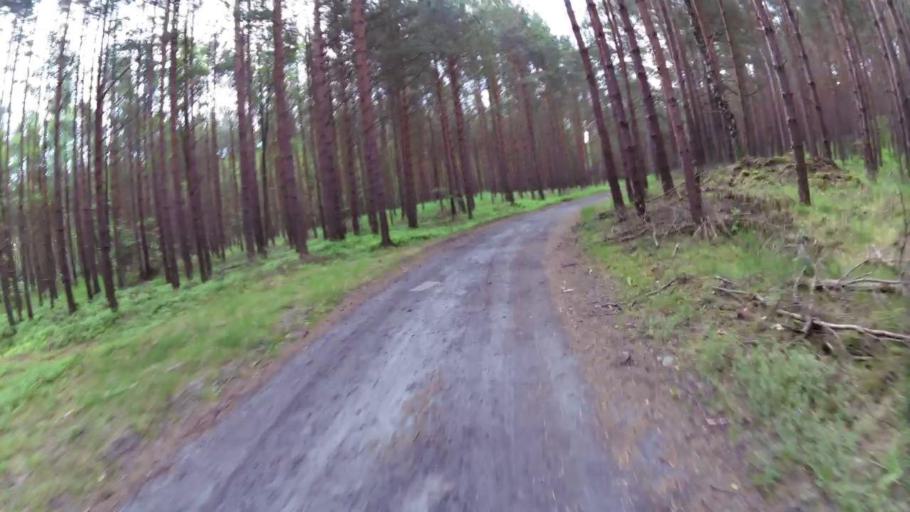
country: PL
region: West Pomeranian Voivodeship
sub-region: Swinoujscie
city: Swinoujscie
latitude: 53.9069
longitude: 14.3270
